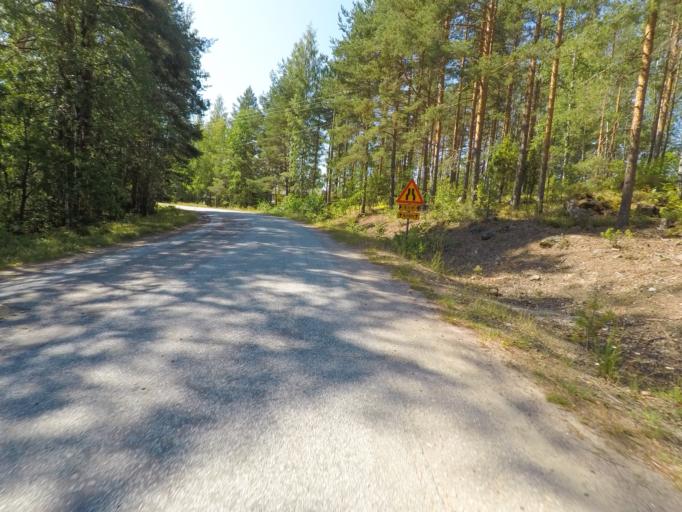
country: FI
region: Southern Savonia
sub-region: Mikkeli
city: Puumala
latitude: 61.4219
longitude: 28.0947
